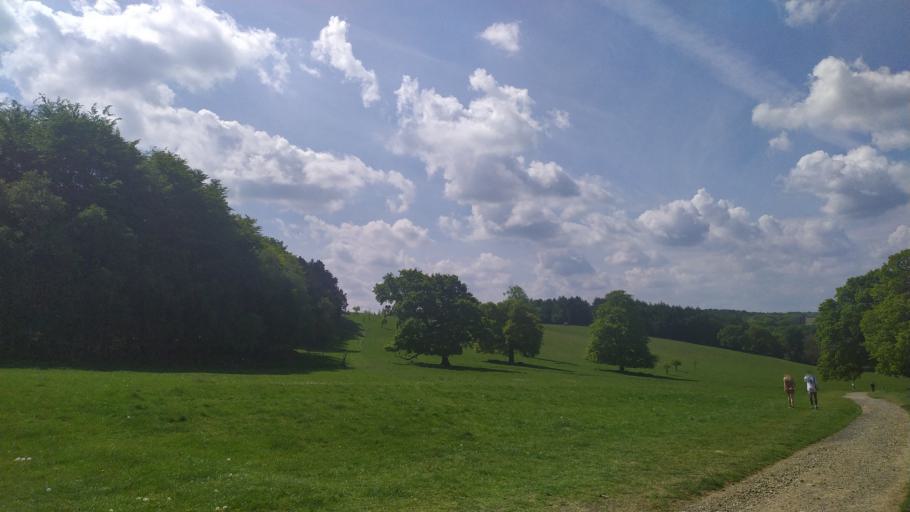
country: GB
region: England
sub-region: City and Borough of Leeds
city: Shadwell
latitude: 53.8845
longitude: -1.5161
